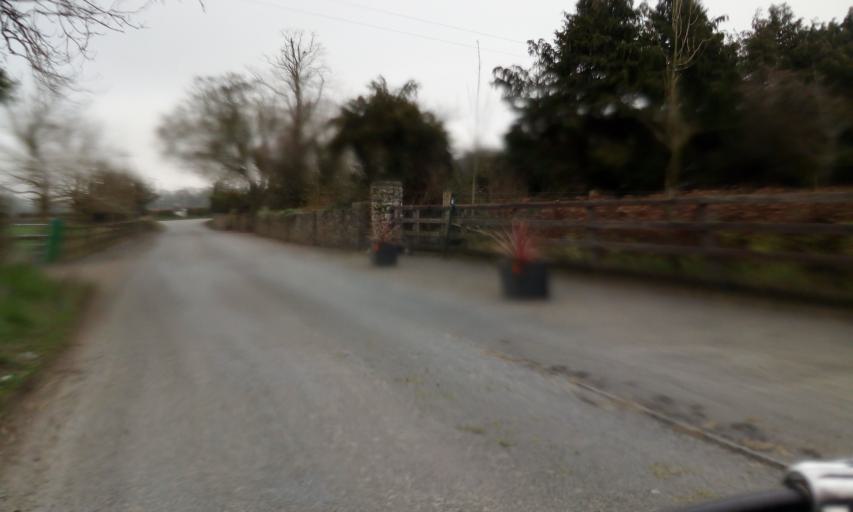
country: IE
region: Leinster
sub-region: Kilkenny
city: Kilkenny
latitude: 52.6592
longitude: -7.1454
